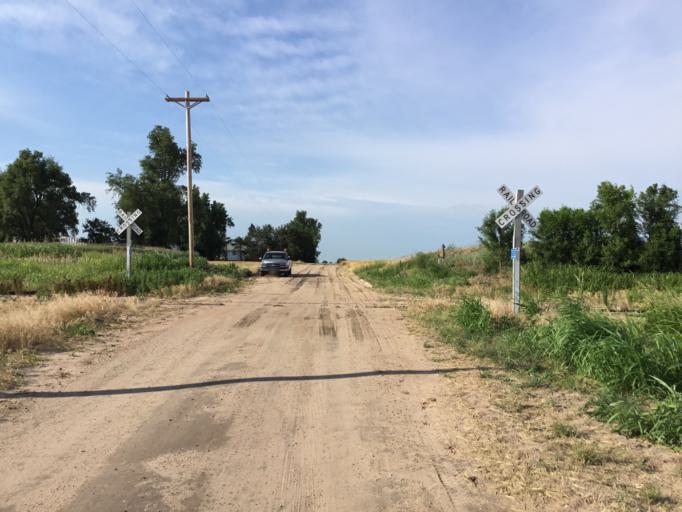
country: US
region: Kansas
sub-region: Barber County
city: Medicine Lodge
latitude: 37.4417
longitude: -98.3917
